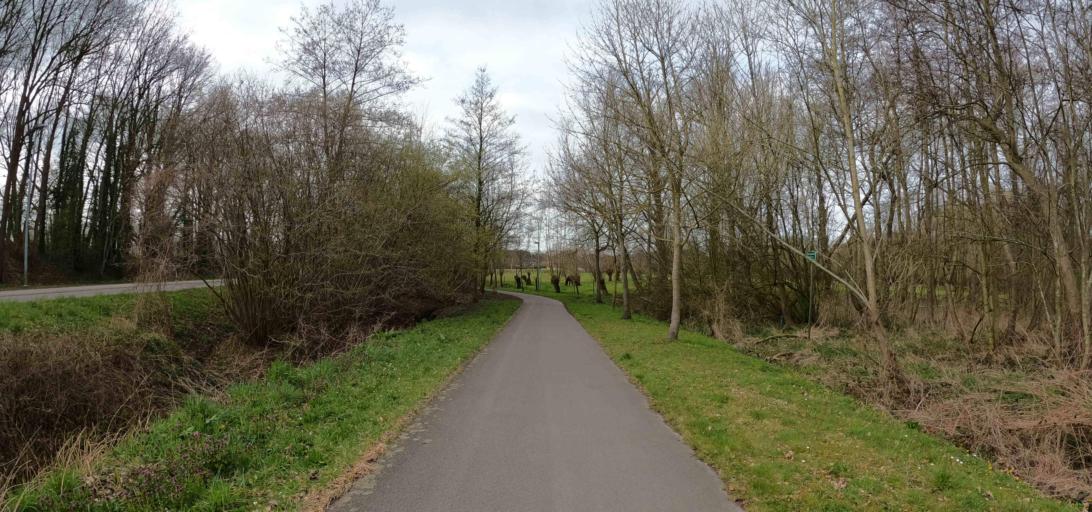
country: BE
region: Flanders
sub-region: Provincie Oost-Vlaanderen
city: Waasmunster
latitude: 51.1146
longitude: 4.1078
